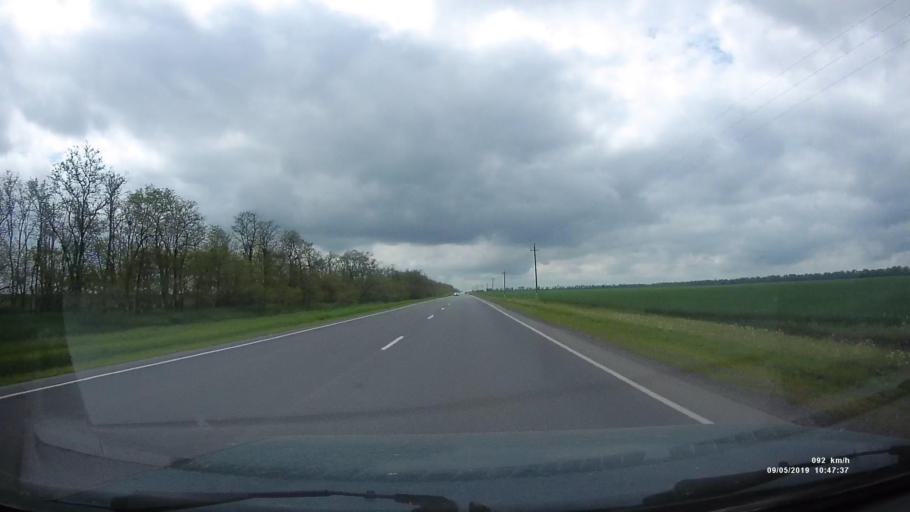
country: RU
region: Rostov
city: Peshkovo
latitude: 46.9683
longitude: 39.3556
